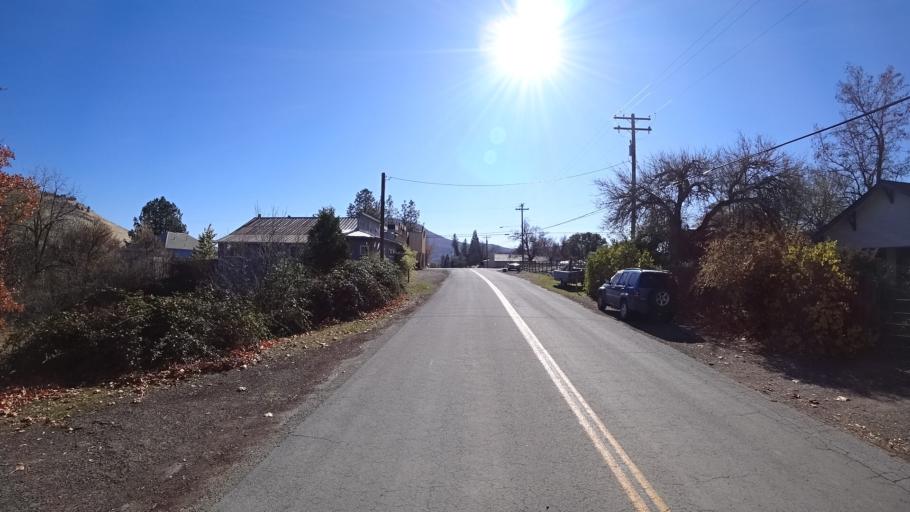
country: US
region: California
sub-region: Siskiyou County
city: Montague
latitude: 41.9096
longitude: -122.5588
